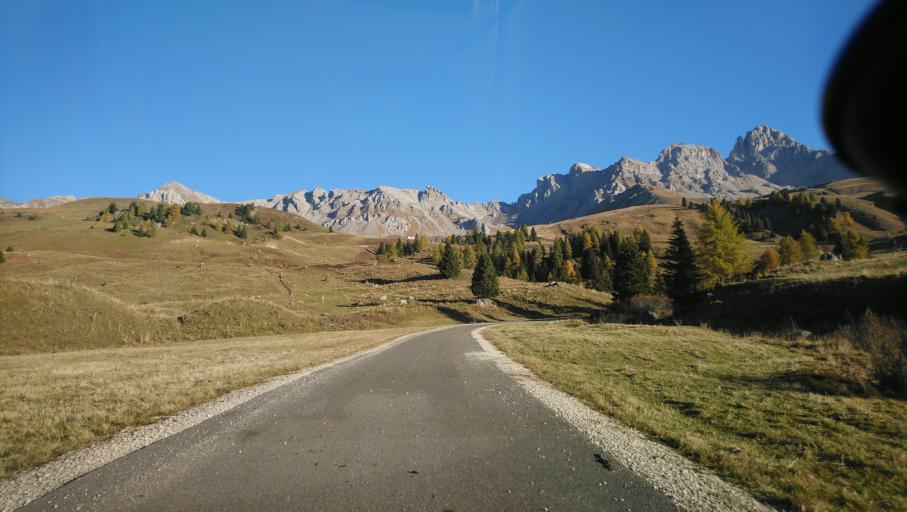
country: IT
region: Veneto
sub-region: Provincia di Belluno
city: Falcade Alto
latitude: 46.3811
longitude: 11.7943
